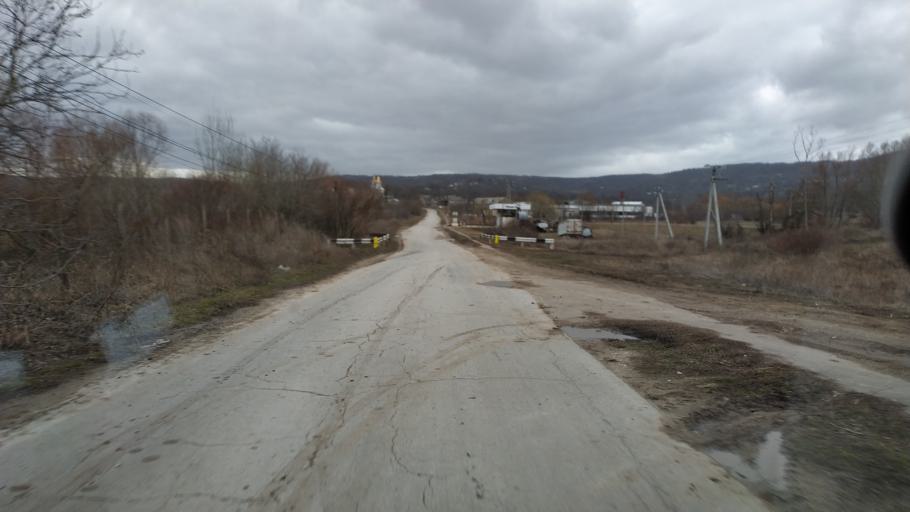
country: MD
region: Calarasi
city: Calarasi
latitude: 47.2542
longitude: 28.1446
